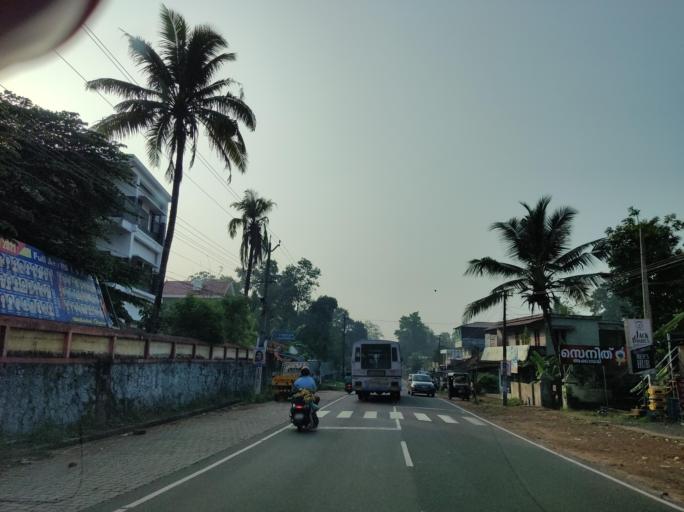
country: IN
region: Kerala
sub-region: Pattanamtitta
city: Adur
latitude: 9.1720
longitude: 76.6498
